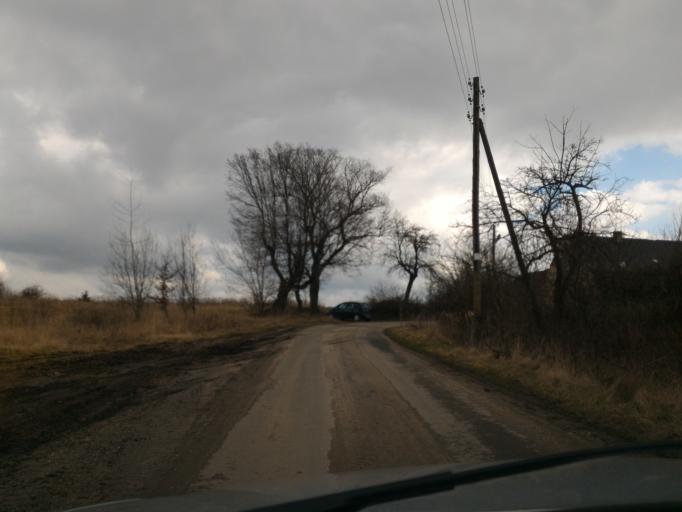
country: PL
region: Lower Silesian Voivodeship
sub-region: Powiat zgorzelecki
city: Bogatynia
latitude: 50.8801
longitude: 14.9014
